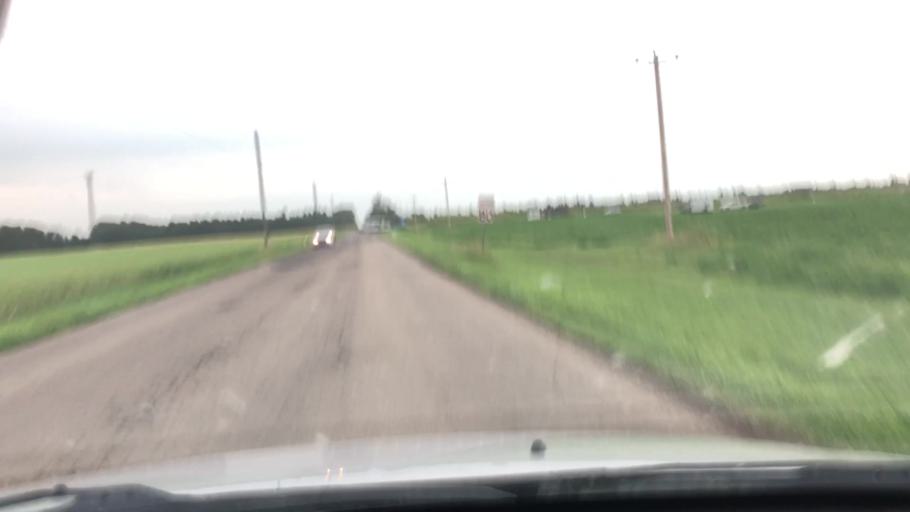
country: CA
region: Alberta
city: Devon
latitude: 53.4241
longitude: -113.6892
